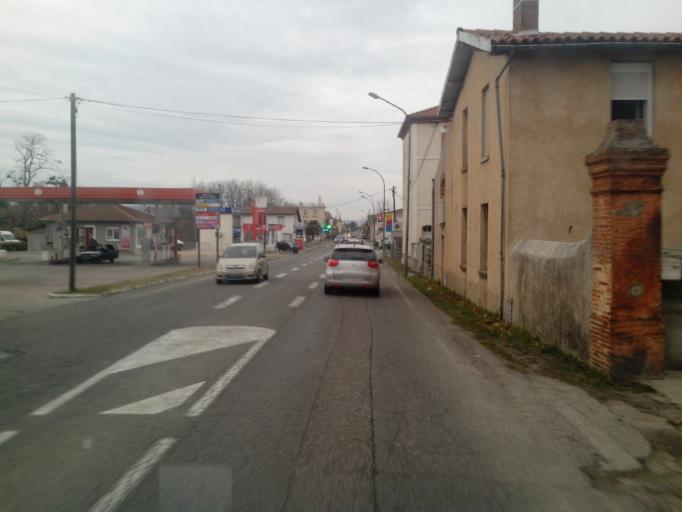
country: FR
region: Midi-Pyrenees
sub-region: Departement de l'Ariege
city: Saint-Jean-du-Falga
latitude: 43.1036
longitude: 1.6208
